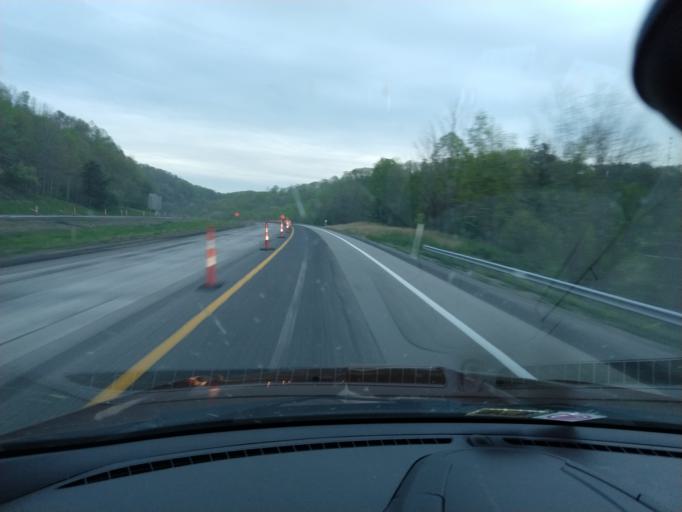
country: US
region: West Virginia
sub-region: Braxton County
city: Sutton
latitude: 38.7210
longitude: -80.6628
